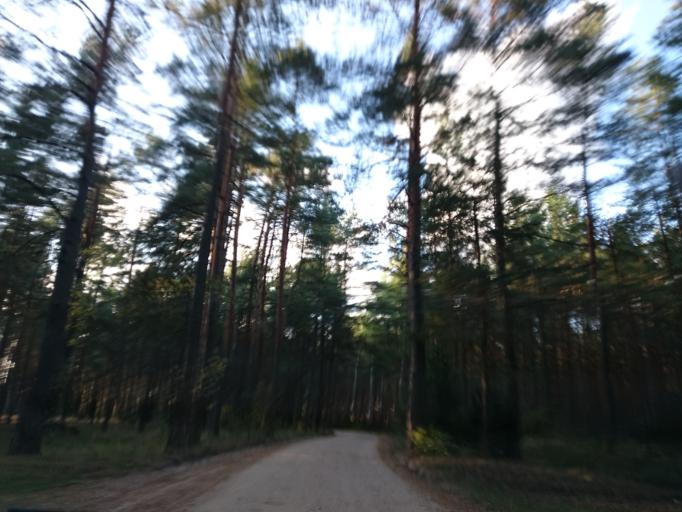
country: LV
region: Adazi
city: Adazi
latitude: 57.0557
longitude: 24.2988
